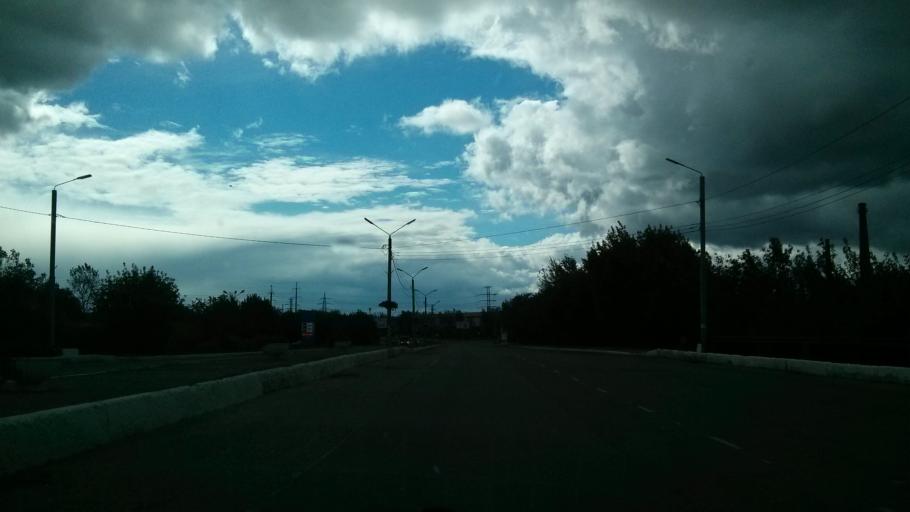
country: RU
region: Vladimir
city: Murom
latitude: 55.5634
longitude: 42.0609
